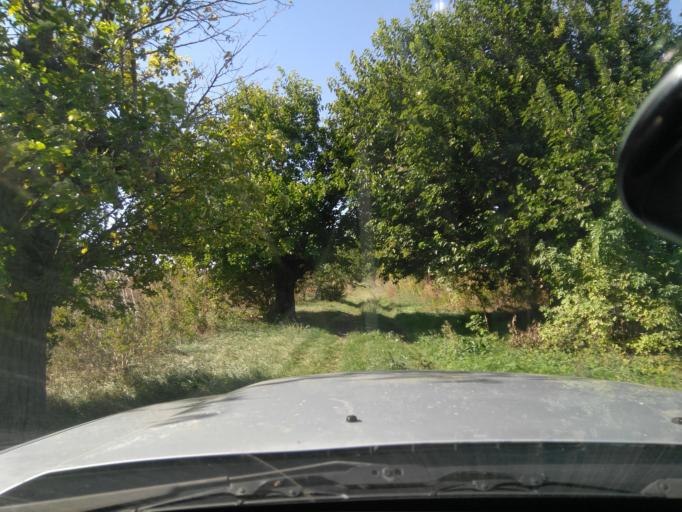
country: HU
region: Fejer
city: Pazmand
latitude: 47.3017
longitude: 18.6972
